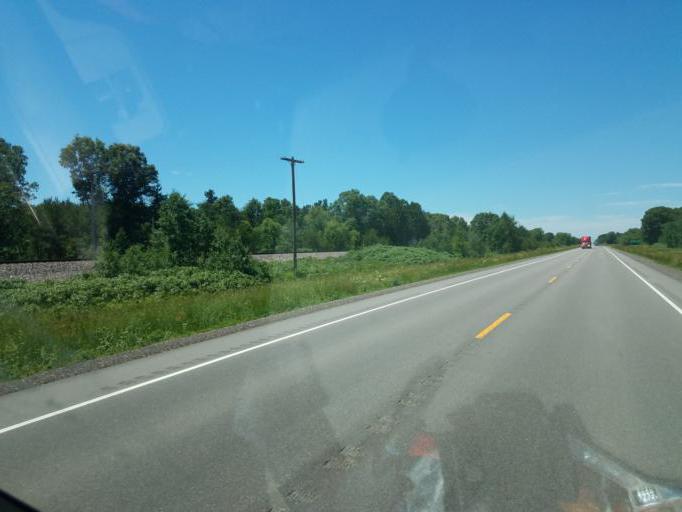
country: US
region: Wisconsin
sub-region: Juneau County
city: New Lisbon
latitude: 44.0248
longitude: -90.1286
